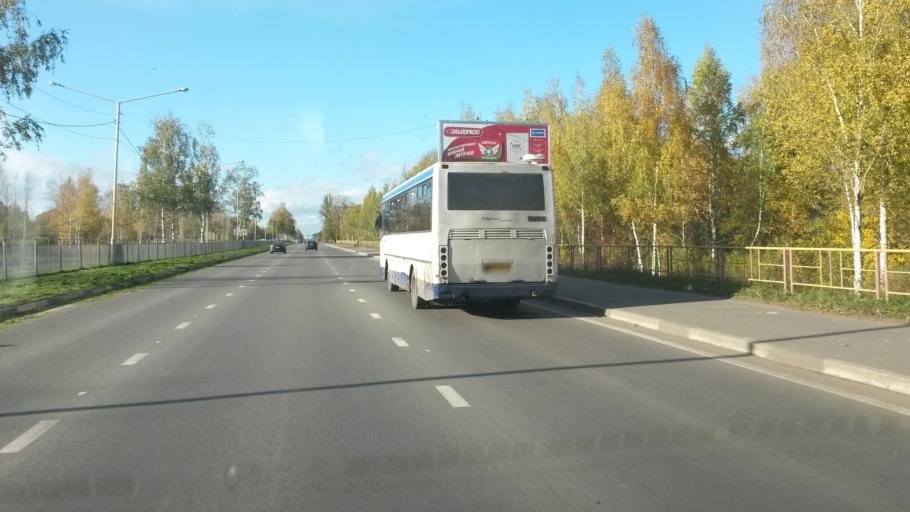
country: RU
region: Jaroslavl
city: Yaroslavl
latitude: 57.5565
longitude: 39.9403
